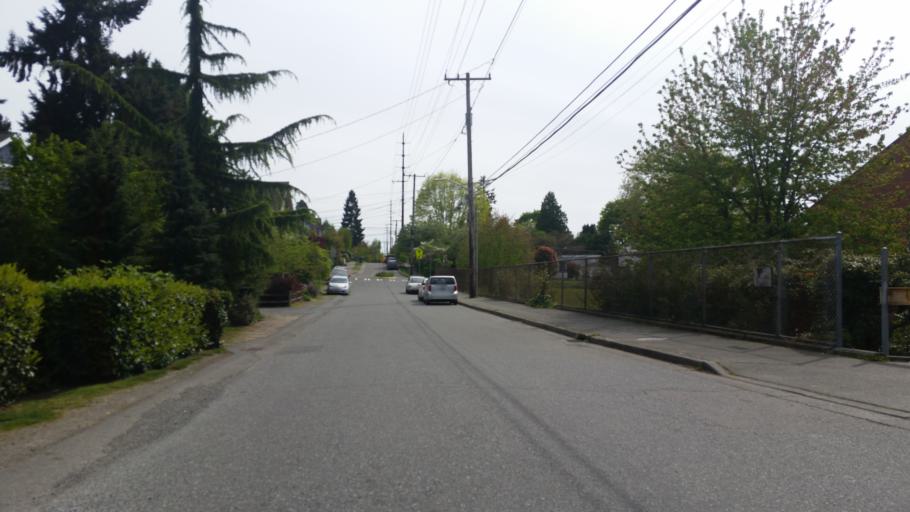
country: US
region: Washington
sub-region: King County
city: Shoreline
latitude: 47.6985
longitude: -122.3204
